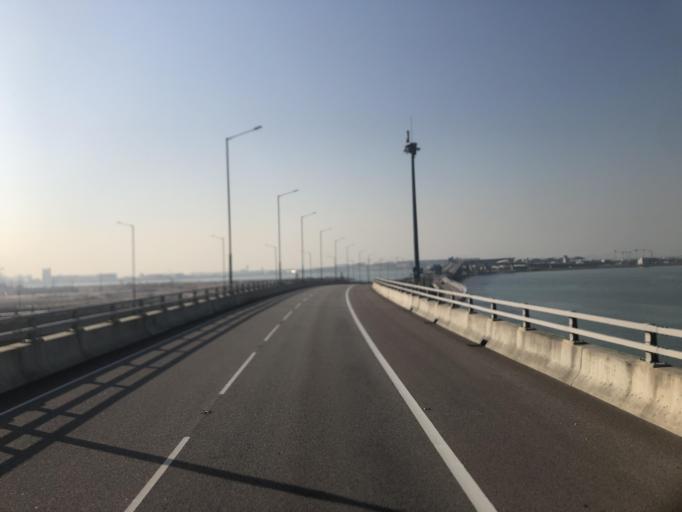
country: HK
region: Tuen Mun
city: Tuen Mun
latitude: 22.3026
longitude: 113.9725
